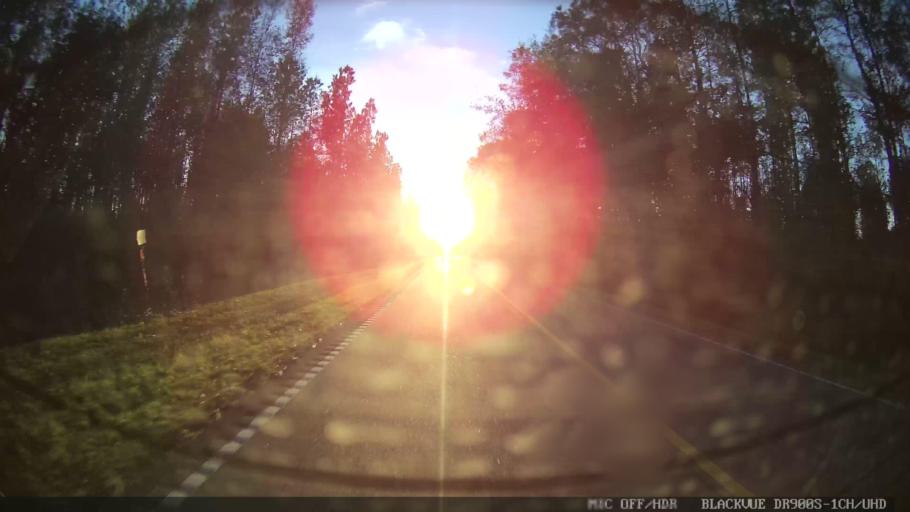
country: US
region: Mississippi
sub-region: Lamar County
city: Lumberton
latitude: 30.9999
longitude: -89.3572
